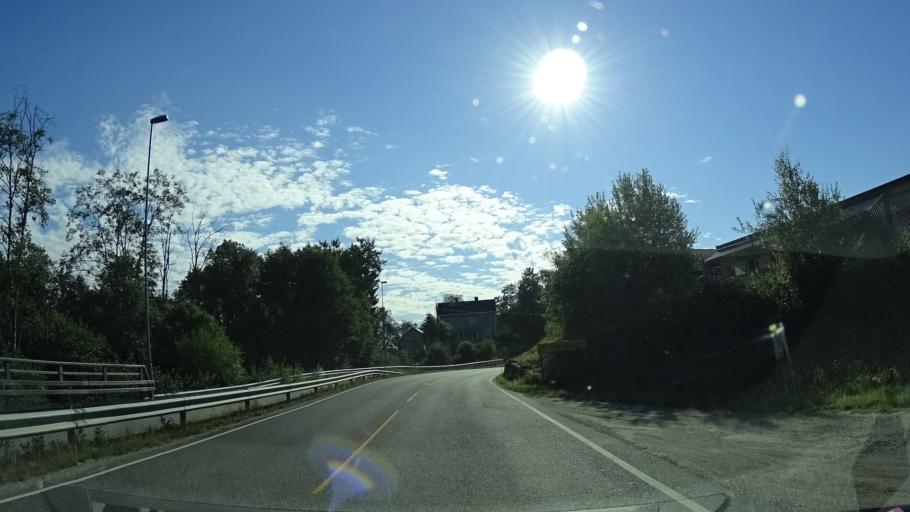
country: NO
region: Ostfold
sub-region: Eidsberg
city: Mysen
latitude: 59.5499
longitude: 11.3526
